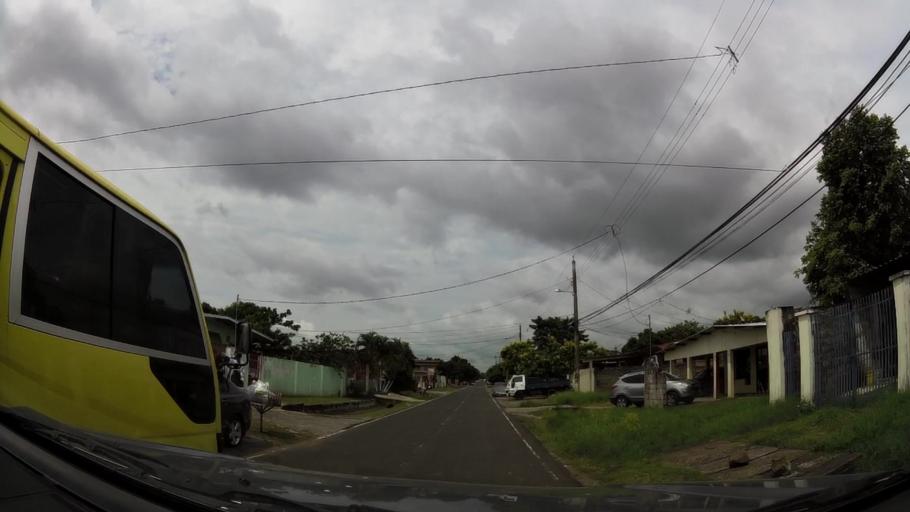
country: PA
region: Panama
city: San Miguelito
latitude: 9.0461
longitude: -79.4228
